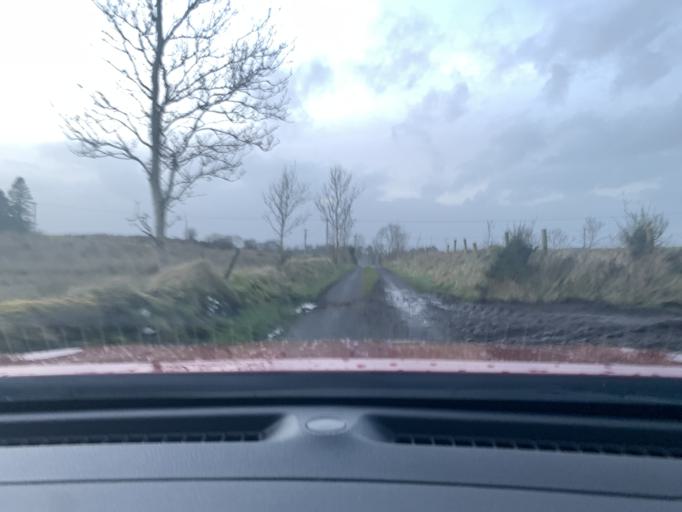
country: IE
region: Connaught
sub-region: Sligo
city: Ballymote
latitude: 53.9916
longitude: -8.4542
